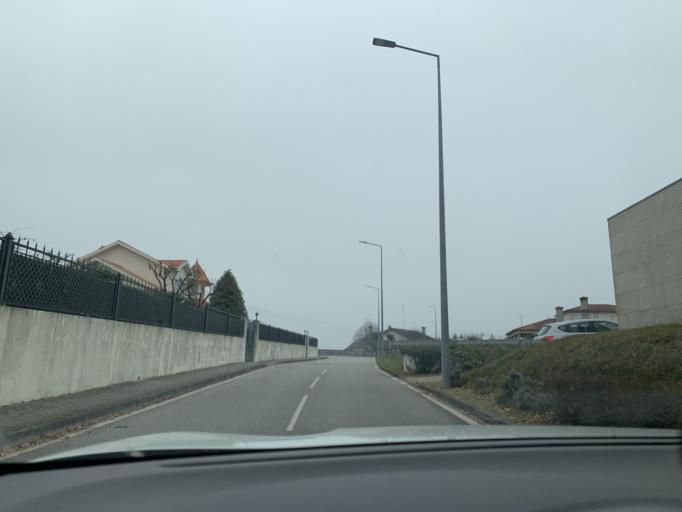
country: PT
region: Viseu
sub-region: Concelho de Tondela
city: Tondela
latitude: 40.5045
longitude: -8.0784
